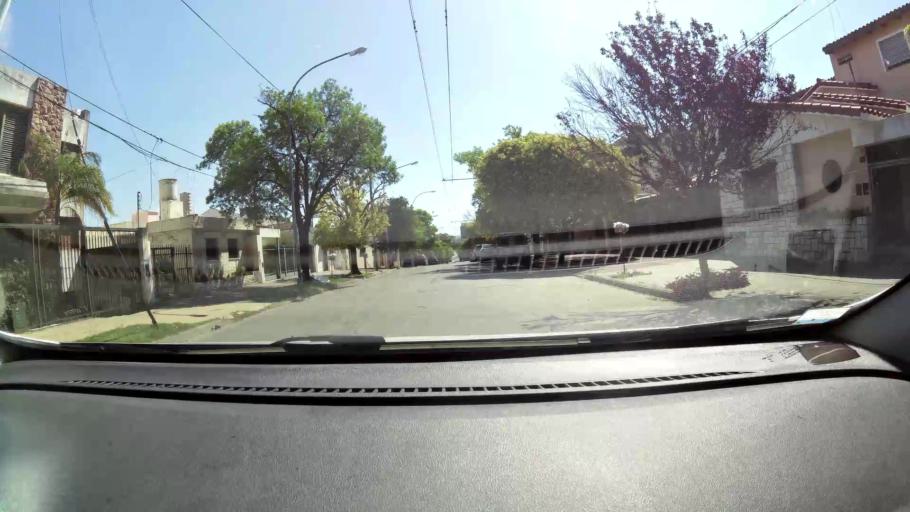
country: AR
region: Cordoba
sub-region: Departamento de Capital
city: Cordoba
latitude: -31.4087
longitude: -64.1602
